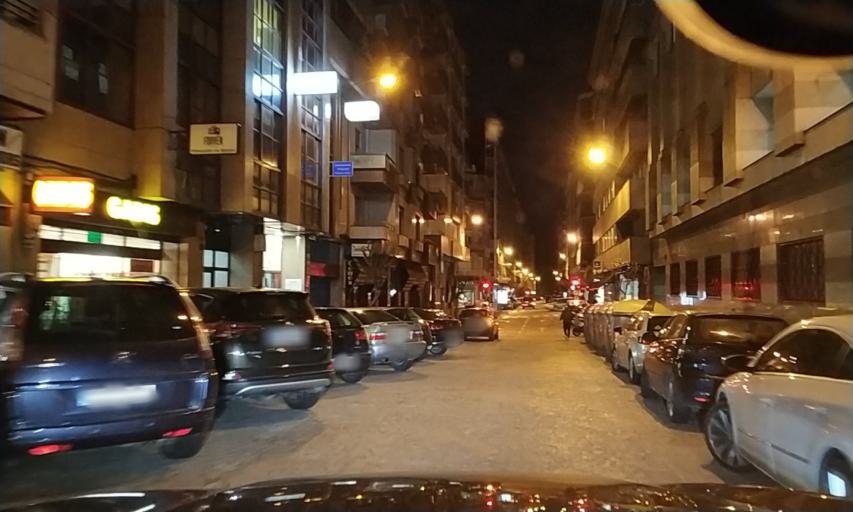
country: ES
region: Galicia
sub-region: Provincia de Ourense
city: Ourense
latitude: 42.3413
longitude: -7.8620
